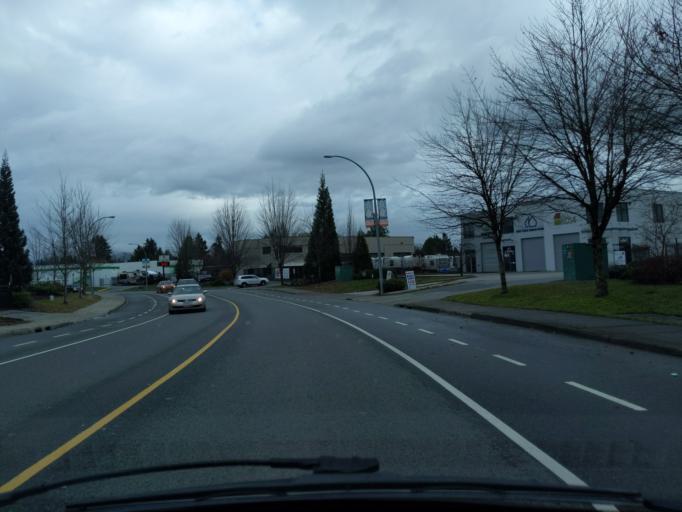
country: CA
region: British Columbia
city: Pitt Meadows
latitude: 49.2093
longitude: -122.6614
